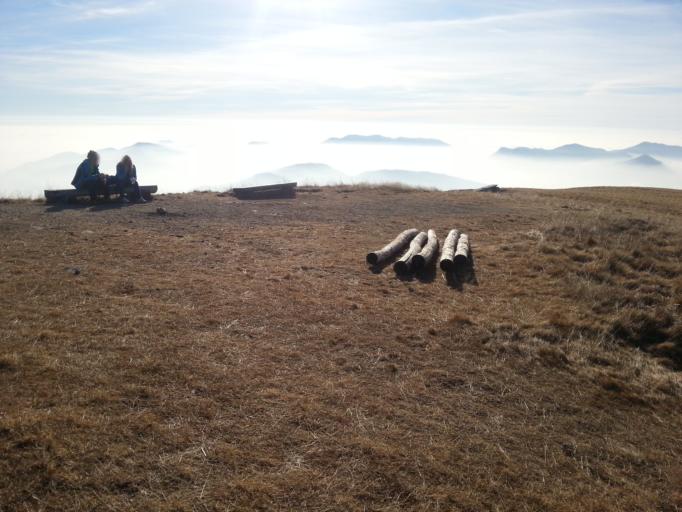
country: IT
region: Lombardy
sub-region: Provincia di Varese
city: Curiglia
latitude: 46.0404
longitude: 8.8320
